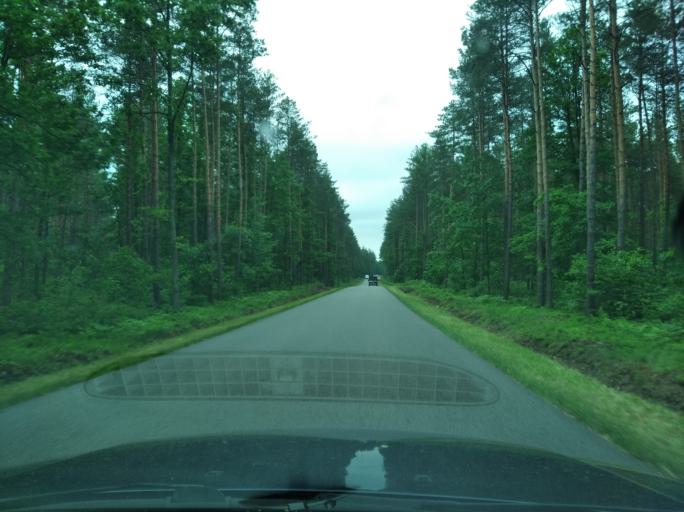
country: PL
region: Subcarpathian Voivodeship
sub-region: Powiat kolbuszowski
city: Niwiska
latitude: 50.1932
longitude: 21.6562
